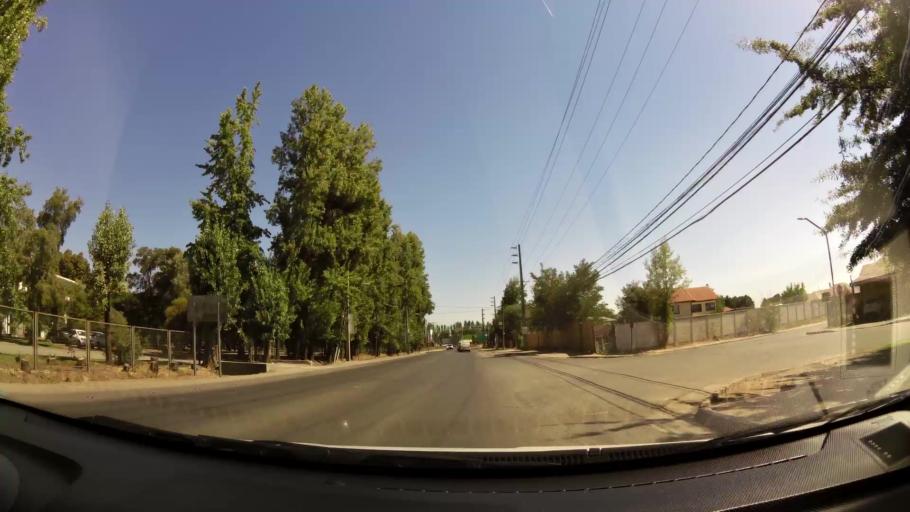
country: CL
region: Maule
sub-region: Provincia de Talca
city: Talca
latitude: -35.4382
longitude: -71.6123
